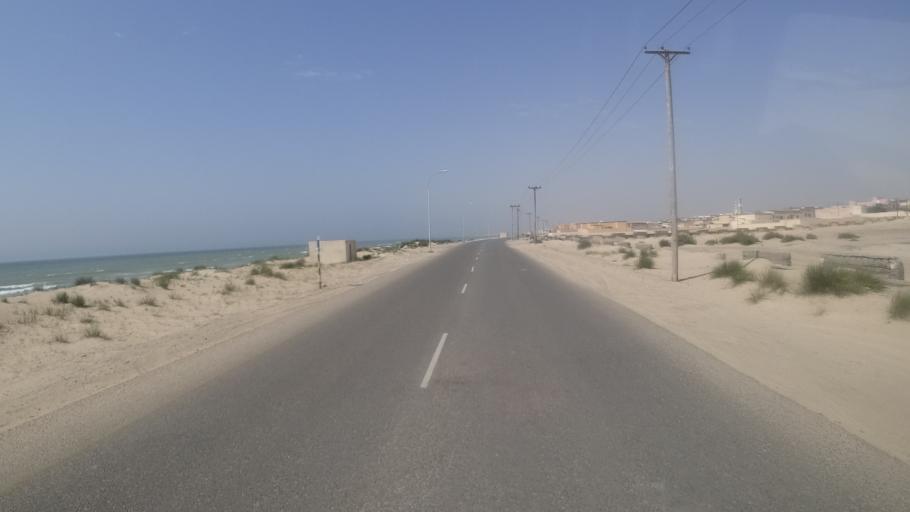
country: OM
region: Ash Sharqiyah
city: Sur
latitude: 22.1232
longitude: 59.7202
